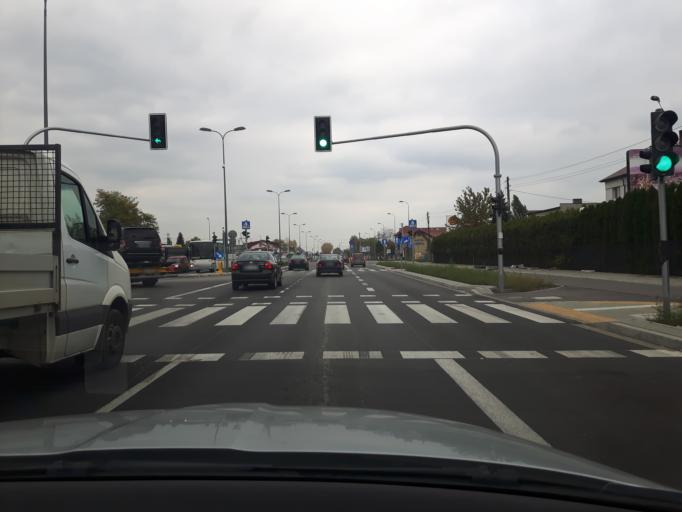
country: PL
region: Masovian Voivodeship
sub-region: Powiat wolominski
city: Zabki
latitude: 52.2865
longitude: 21.0855
